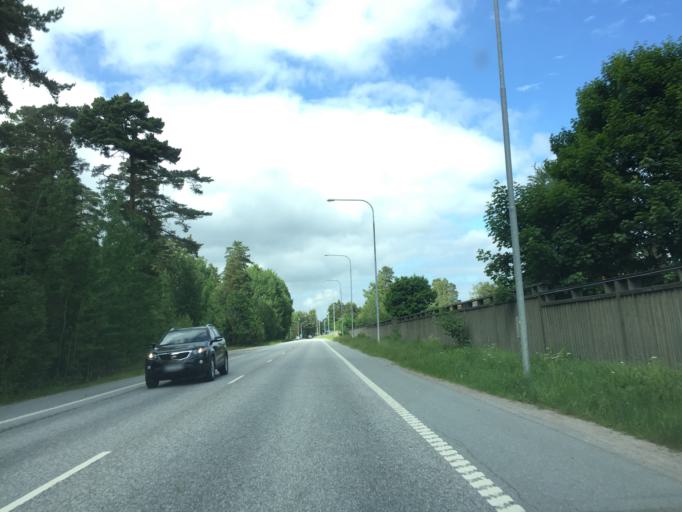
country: SE
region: OErebro
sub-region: Orebro Kommun
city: Orebro
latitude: 59.2226
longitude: 15.1463
